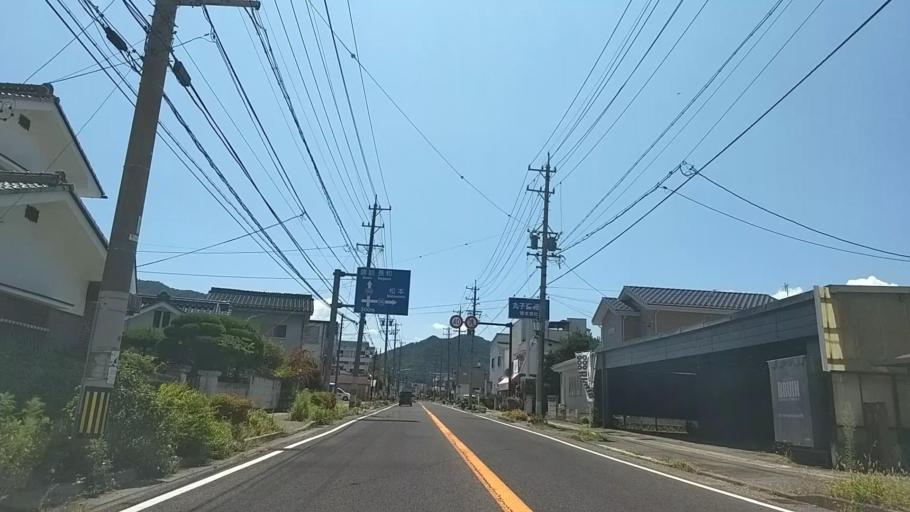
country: JP
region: Nagano
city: Kamimaruko
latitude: 36.3263
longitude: 138.2700
